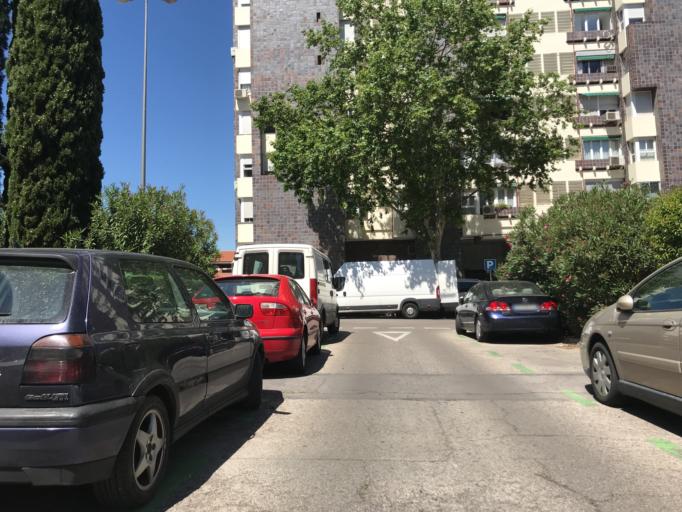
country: ES
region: Madrid
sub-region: Provincia de Madrid
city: Retiro
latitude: 40.4152
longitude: -3.6742
